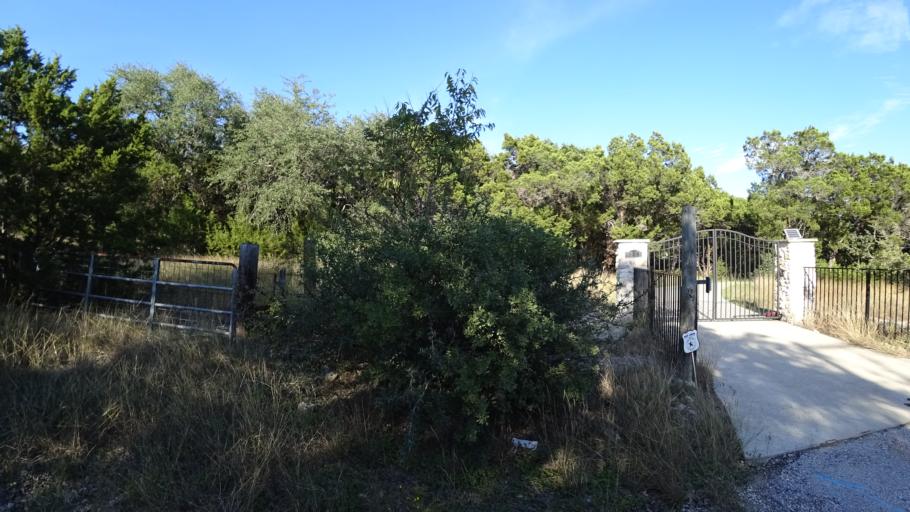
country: US
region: Texas
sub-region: Travis County
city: Barton Creek
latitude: 30.2447
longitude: -97.9051
